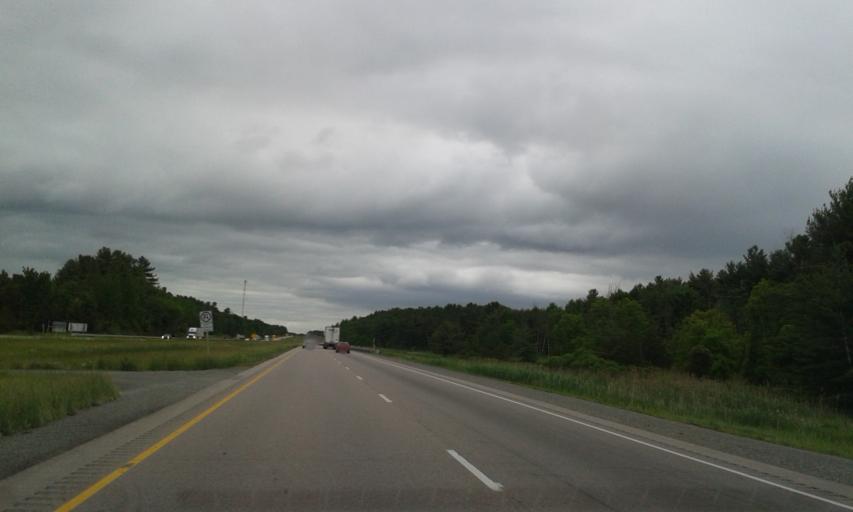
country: US
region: New York
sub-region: Jefferson County
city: Alexandria Bay
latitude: 44.4921
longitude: -75.8519
